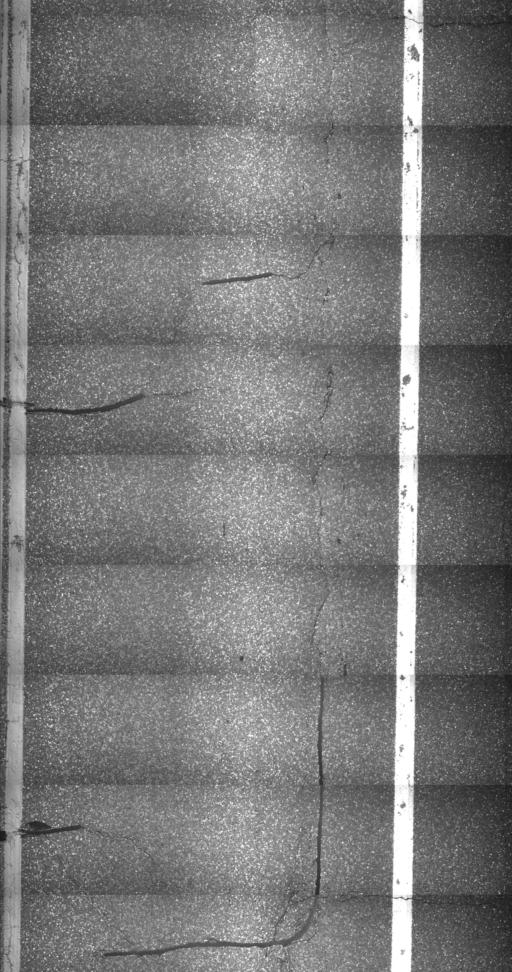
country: US
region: New Hampshire
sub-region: Grafton County
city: Lyme
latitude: 43.8085
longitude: -72.1895
